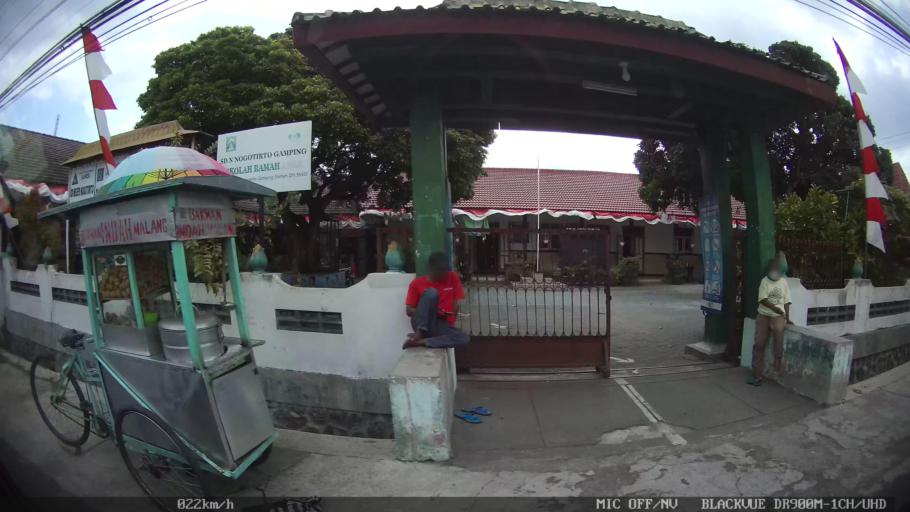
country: ID
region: Daerah Istimewa Yogyakarta
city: Yogyakarta
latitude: -7.7705
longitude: 110.3383
